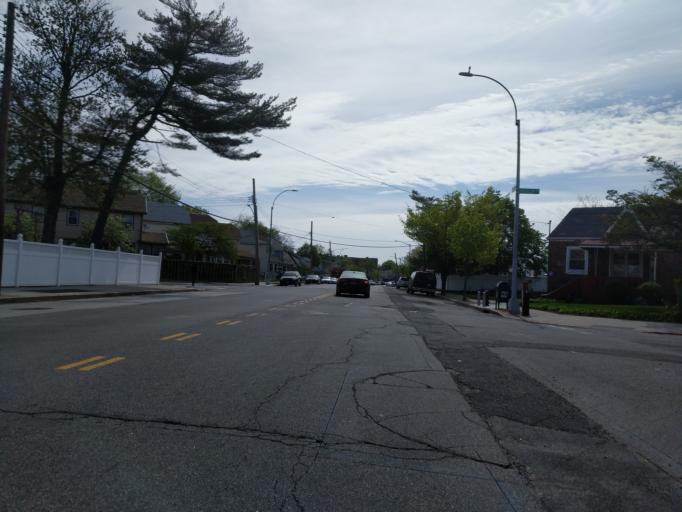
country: US
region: New York
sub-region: Queens County
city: Jamaica
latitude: 40.7042
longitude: -73.7700
